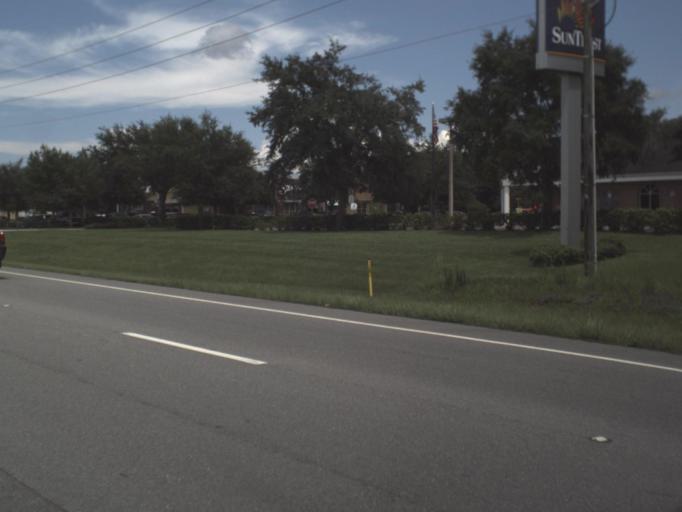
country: US
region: Florida
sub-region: Pasco County
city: Wesley Chapel
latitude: 28.2341
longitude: -82.3503
